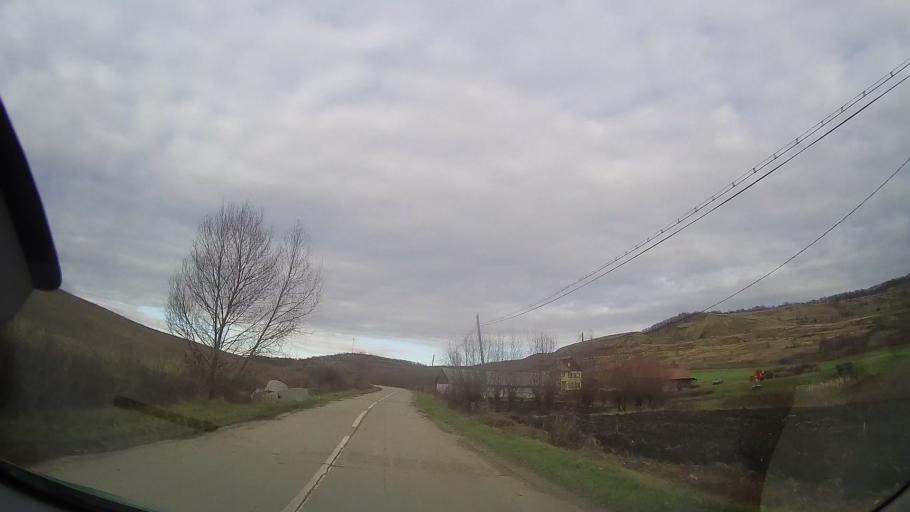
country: RO
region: Bistrita-Nasaud
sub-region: Comuna Micestii de Campie
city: Micestii de Campie
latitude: 46.8384
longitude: 24.3044
